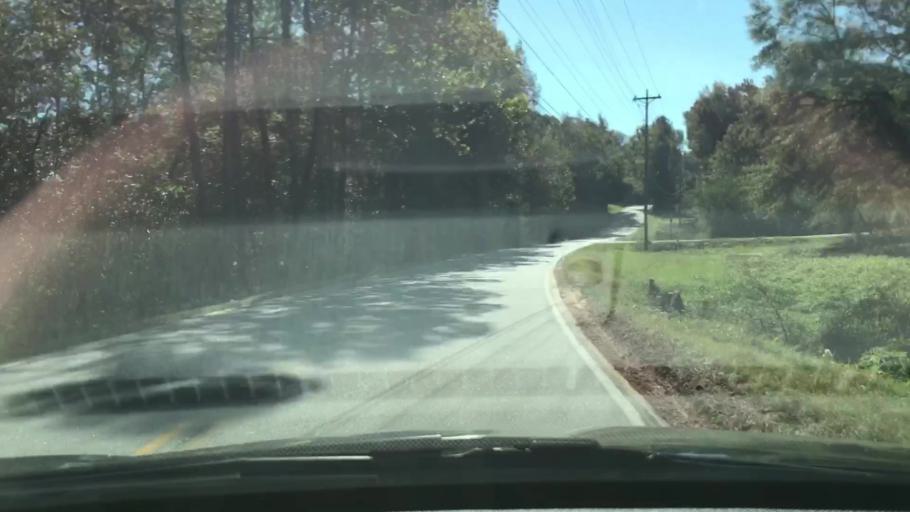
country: US
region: Georgia
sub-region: Carroll County
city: Villa Rica
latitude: 33.7443
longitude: -84.9078
